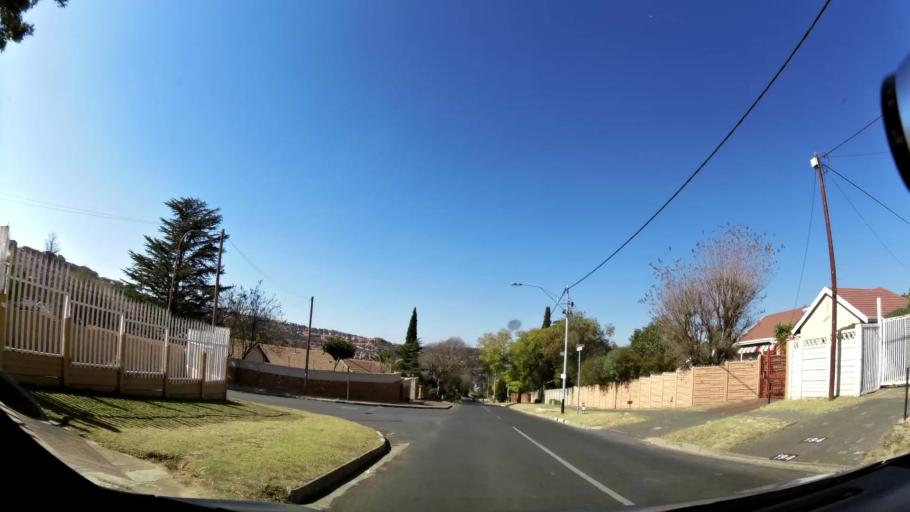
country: ZA
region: Gauteng
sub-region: City of Johannesburg Metropolitan Municipality
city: Johannesburg
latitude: -26.2682
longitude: 28.0040
